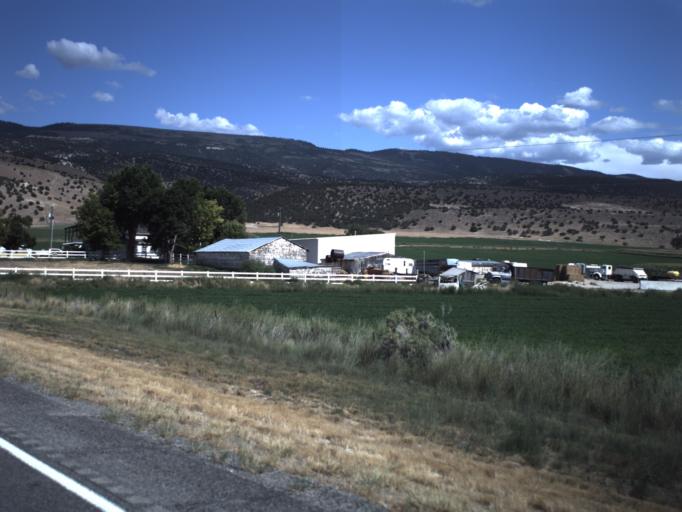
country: US
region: Utah
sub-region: Sanpete County
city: Gunnison
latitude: 39.1691
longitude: -111.7115
